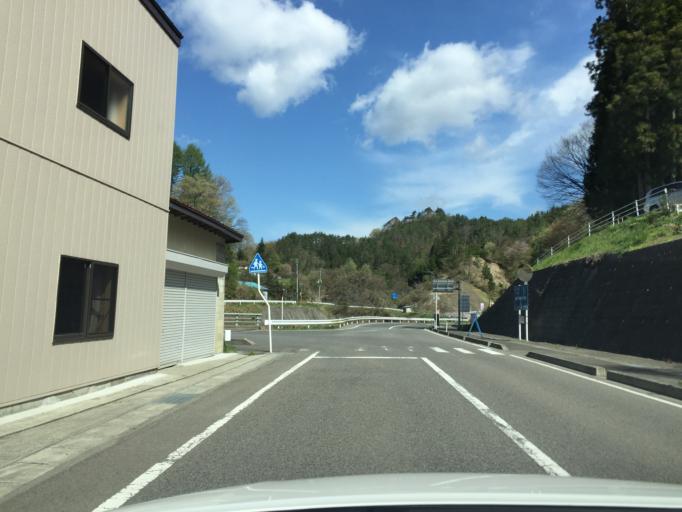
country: JP
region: Fukushima
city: Funehikimachi-funehiki
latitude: 37.5312
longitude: 140.6098
